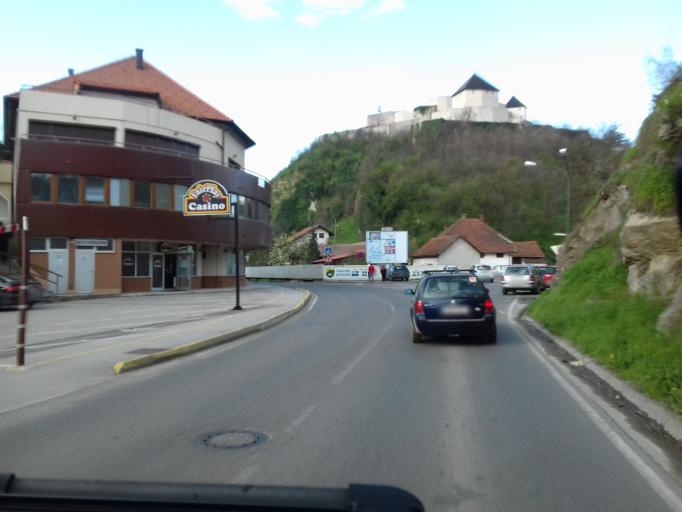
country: BA
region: Federation of Bosnia and Herzegovina
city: Tesanj
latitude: 44.6153
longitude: 17.9914
